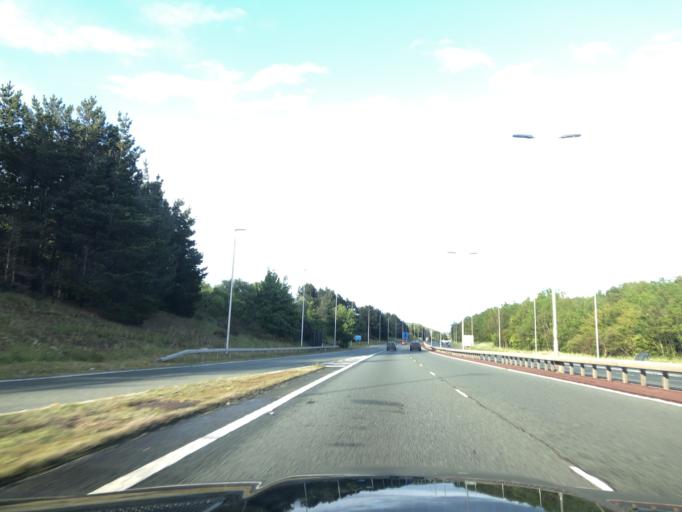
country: GB
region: Wales
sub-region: Conwy
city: Conwy
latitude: 53.2894
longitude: -3.8490
